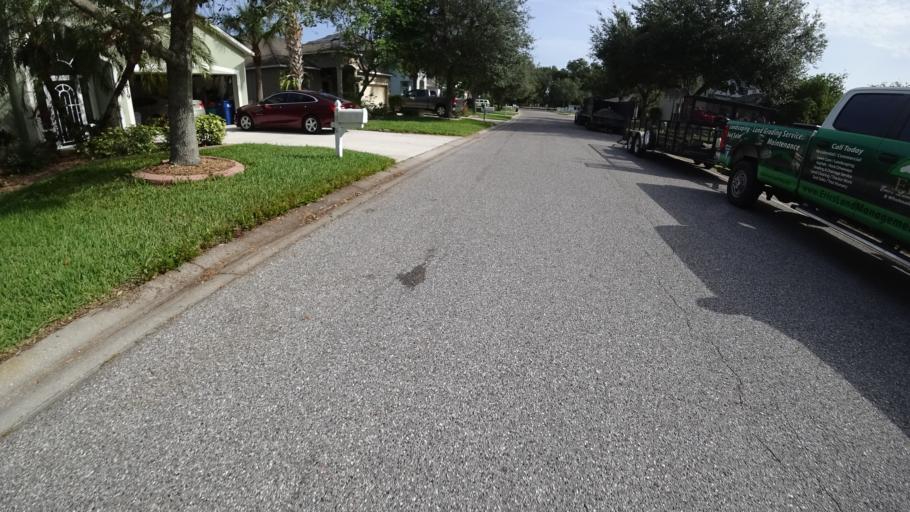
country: US
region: Florida
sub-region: Manatee County
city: Ellenton
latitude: 27.5568
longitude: -82.4970
